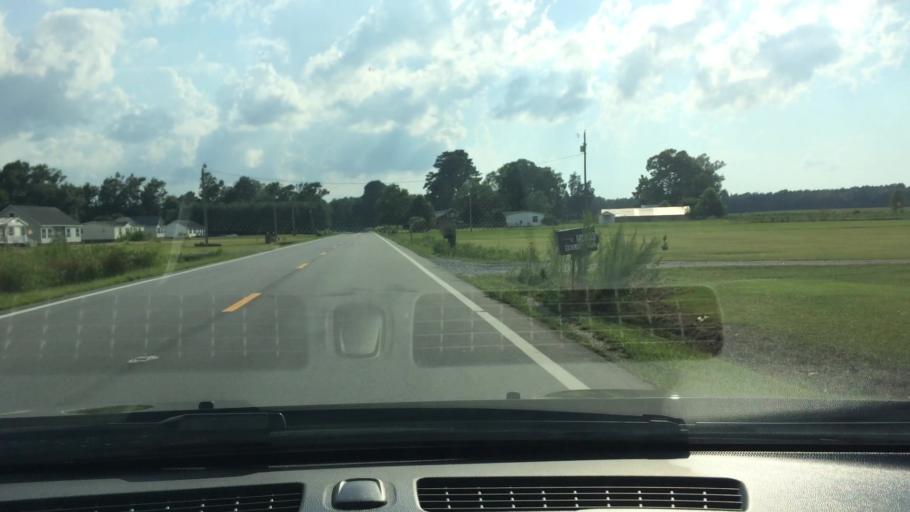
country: US
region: North Carolina
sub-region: Craven County
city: Vanceboro
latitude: 35.4378
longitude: -77.1574
